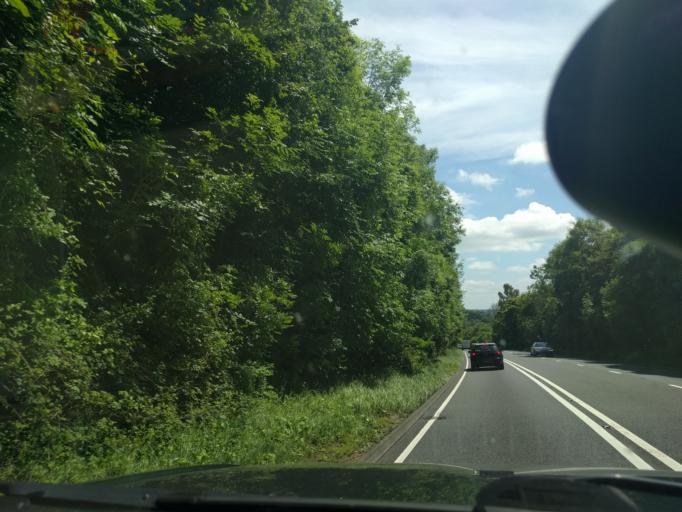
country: GB
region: England
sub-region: South Gloucestershire
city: Cold Ashton
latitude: 51.4175
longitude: -2.3503
